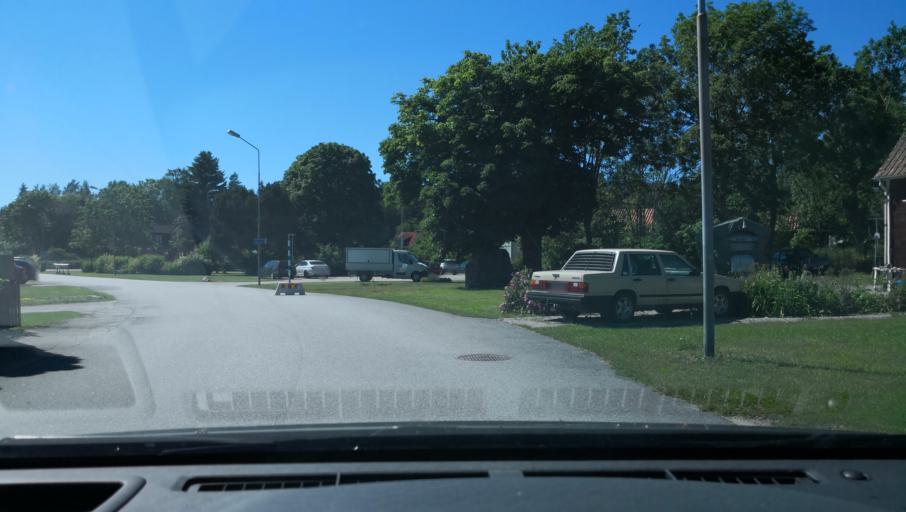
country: SE
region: Vaestmanland
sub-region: Kungsors Kommun
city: Kungsoer
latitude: 59.2828
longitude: 16.1156
